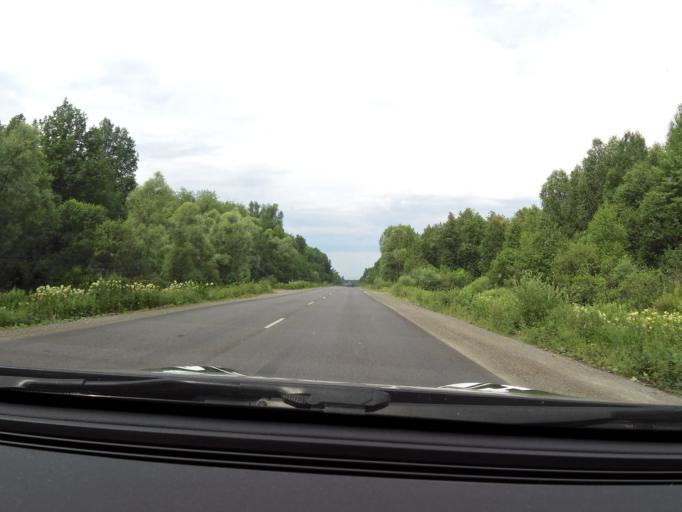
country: RU
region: Chelyabinsk
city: Asha
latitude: 54.8781
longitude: 57.2193
